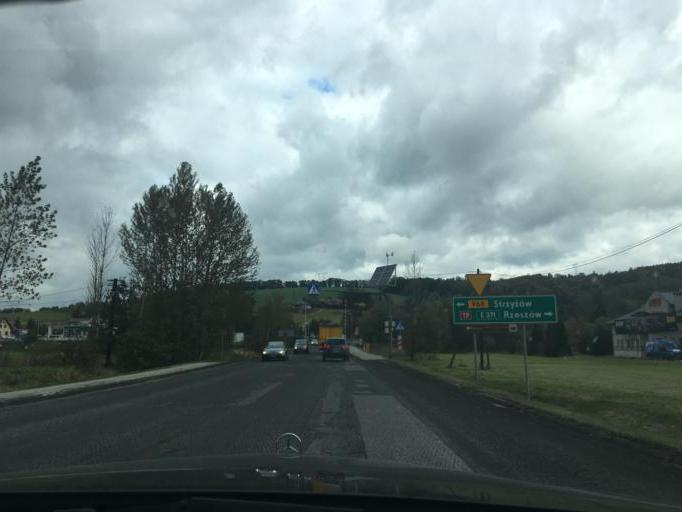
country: PL
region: Subcarpathian Voivodeship
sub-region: Powiat strzyzowski
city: Babica
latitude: 49.9323
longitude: 21.8716
